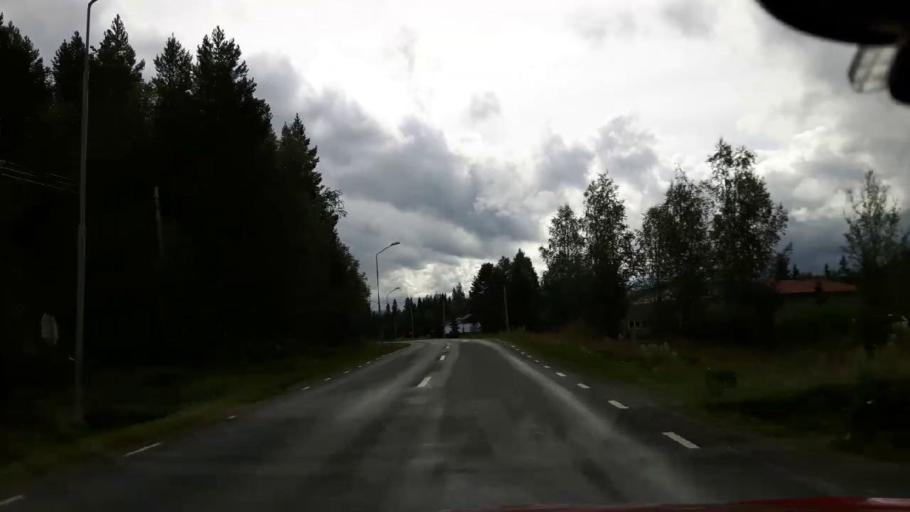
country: NO
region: Nord-Trondelag
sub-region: Lierne
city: Sandvika
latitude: 64.5064
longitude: 14.1572
